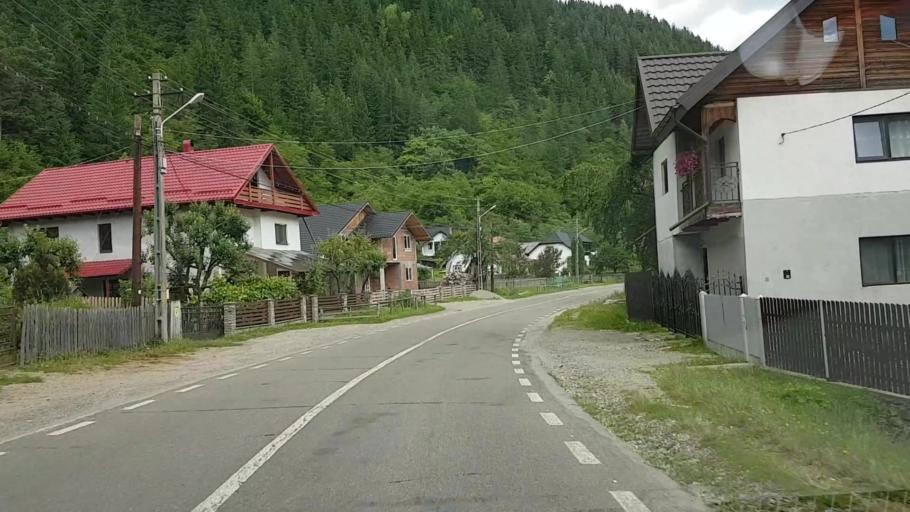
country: RO
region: Suceava
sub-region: Comuna Brosteni
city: Brosteni
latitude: 47.2363
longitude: 25.7329
